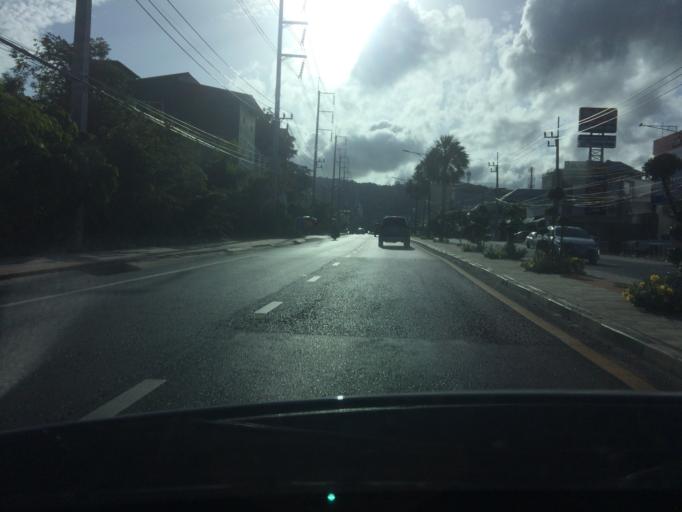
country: TH
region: Phuket
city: Mueang Phuket
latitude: 7.8725
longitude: 98.3687
